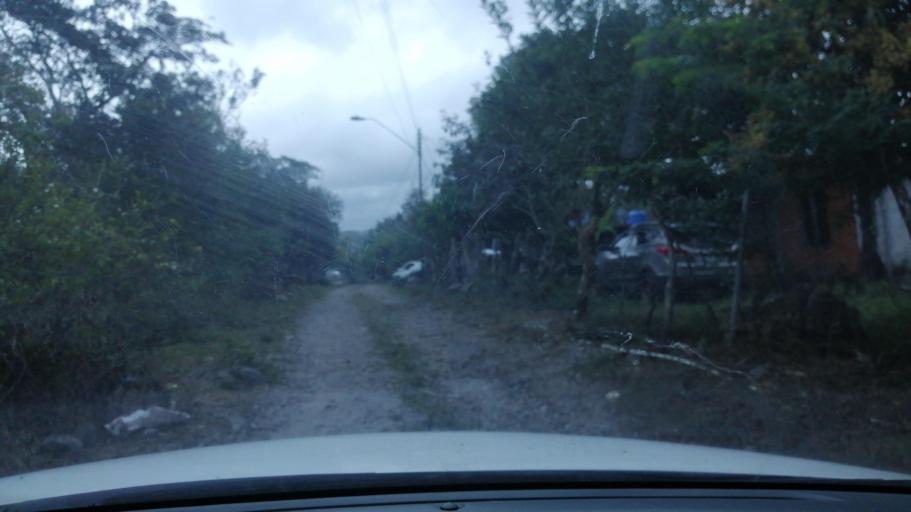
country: PA
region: Chiriqui
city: Potrerillos Arriba
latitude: 8.6865
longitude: -82.4527
